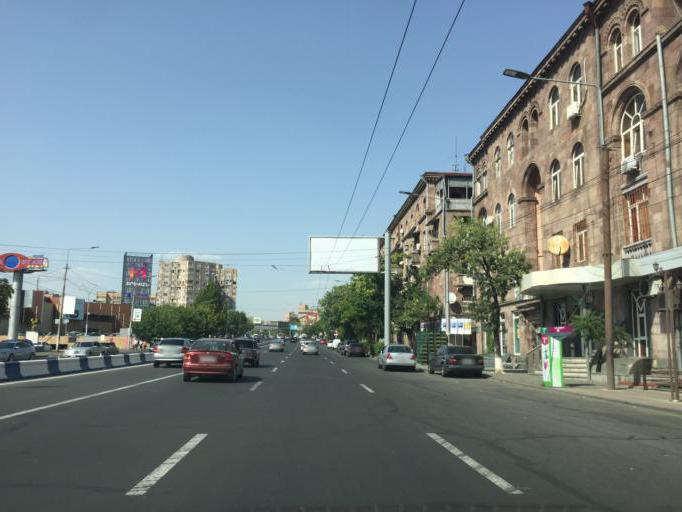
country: AM
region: Yerevan
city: Yerevan
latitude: 40.1535
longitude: 44.4995
